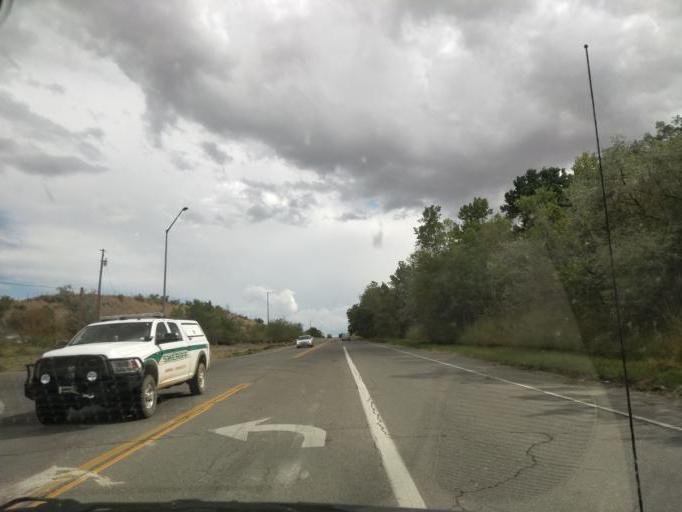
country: US
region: Colorado
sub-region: Mesa County
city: Clifton
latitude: 39.0536
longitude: -108.4596
